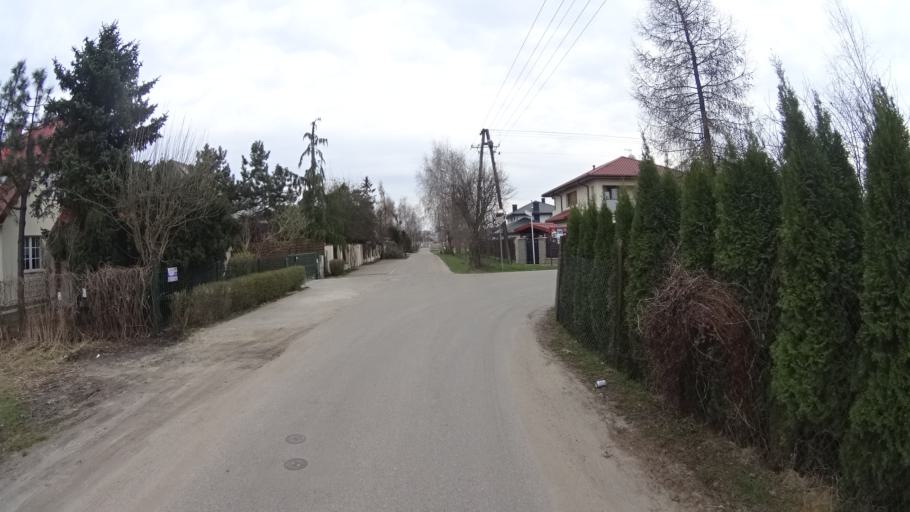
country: PL
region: Masovian Voivodeship
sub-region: Powiat warszawski zachodni
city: Jozefow
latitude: 52.2026
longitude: 20.6929
